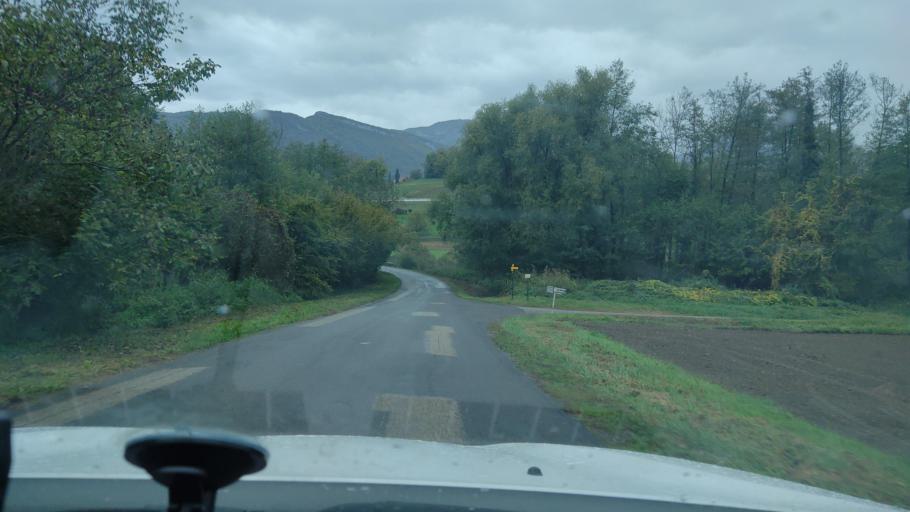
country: FR
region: Rhone-Alpes
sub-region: Departement de la Savoie
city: Cruet
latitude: 45.5002
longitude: 6.1087
